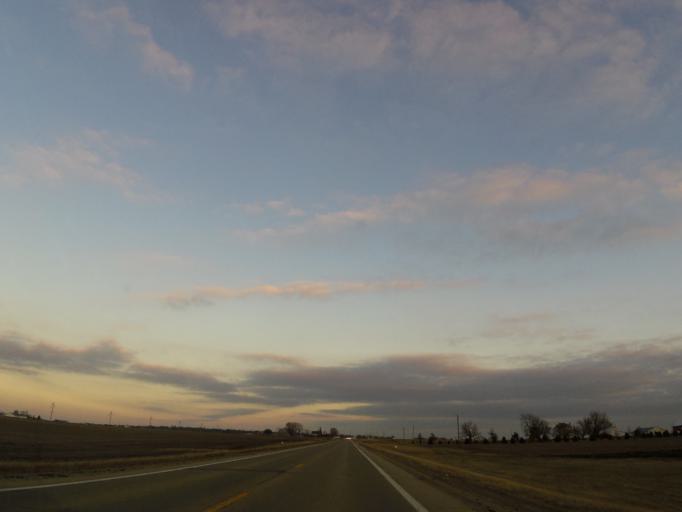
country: US
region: Illinois
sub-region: McLean County
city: Gridley
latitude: 40.7392
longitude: -88.9141
